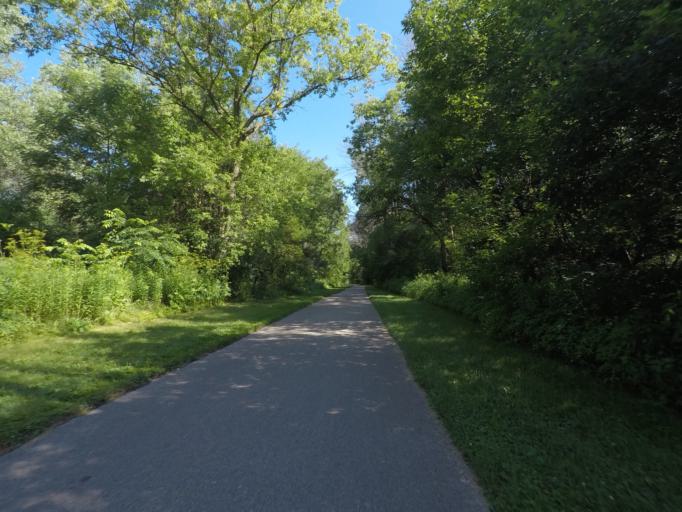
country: US
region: Wisconsin
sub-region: Waukesha County
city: Elm Grove
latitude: 43.0326
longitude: -88.0681
